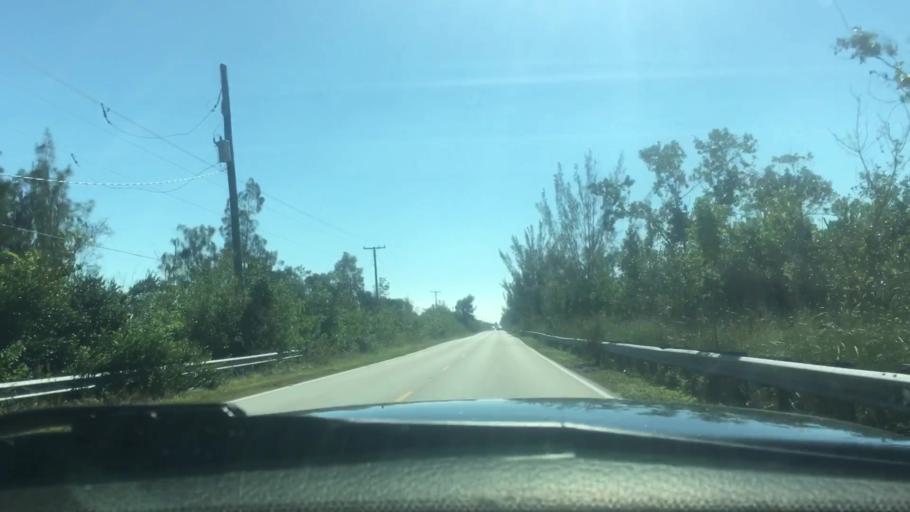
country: US
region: Florida
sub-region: Miami-Dade County
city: Florida City
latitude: 25.3638
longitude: -80.4279
